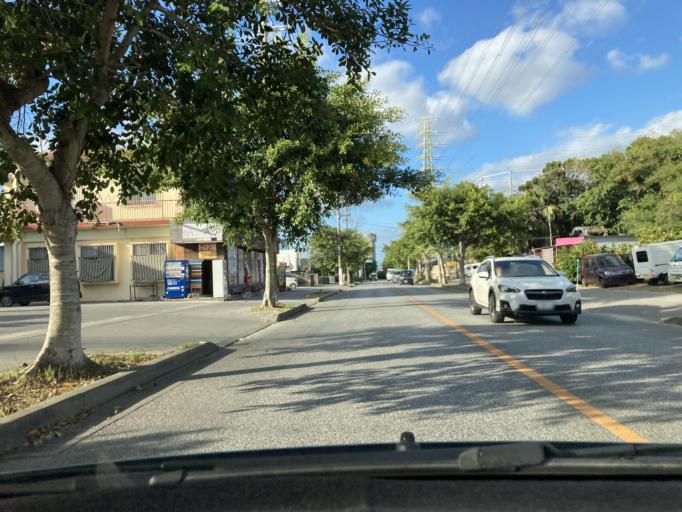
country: JP
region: Okinawa
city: Gushikawa
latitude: 26.3569
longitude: 127.8634
